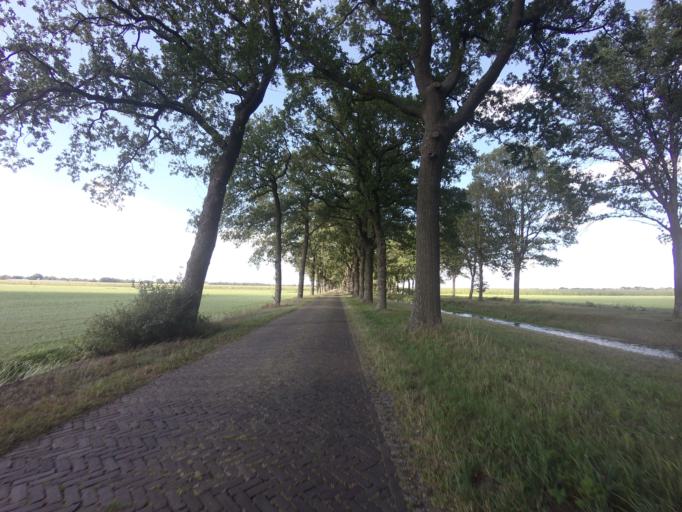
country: NL
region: Drenthe
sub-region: Gemeente Hoogeveen
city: Hoogeveen
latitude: 52.6552
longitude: 6.5143
